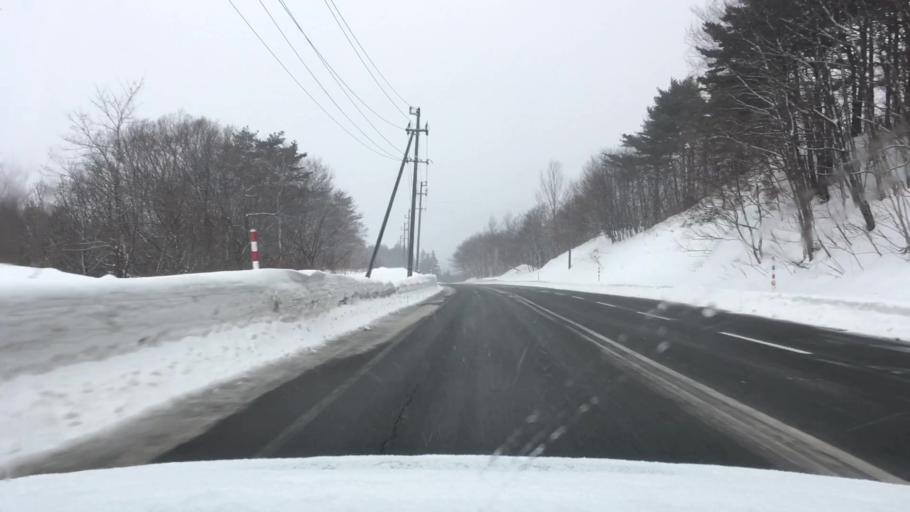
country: JP
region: Akita
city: Hanawa
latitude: 40.0205
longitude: 140.9882
